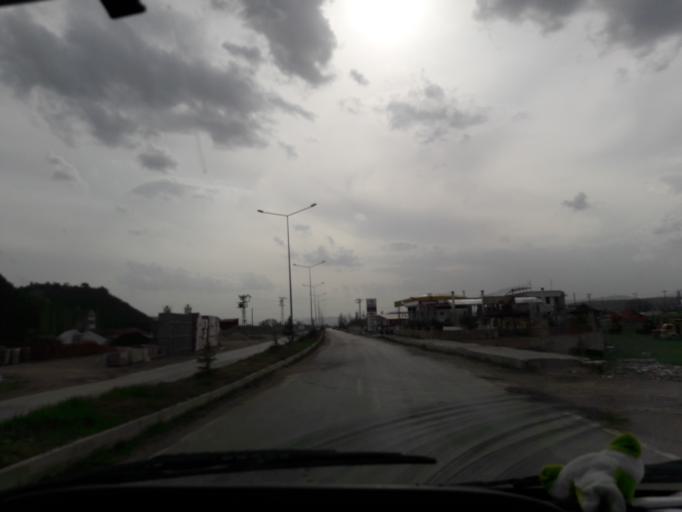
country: TR
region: Gumushane
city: Siran
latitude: 40.1793
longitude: 39.1192
